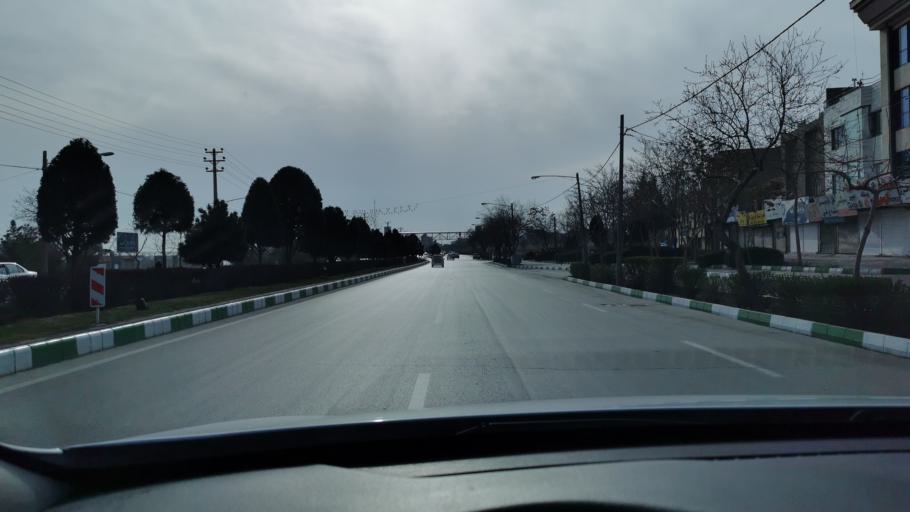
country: IR
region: Razavi Khorasan
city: Mashhad
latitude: 36.3024
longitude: 59.5172
